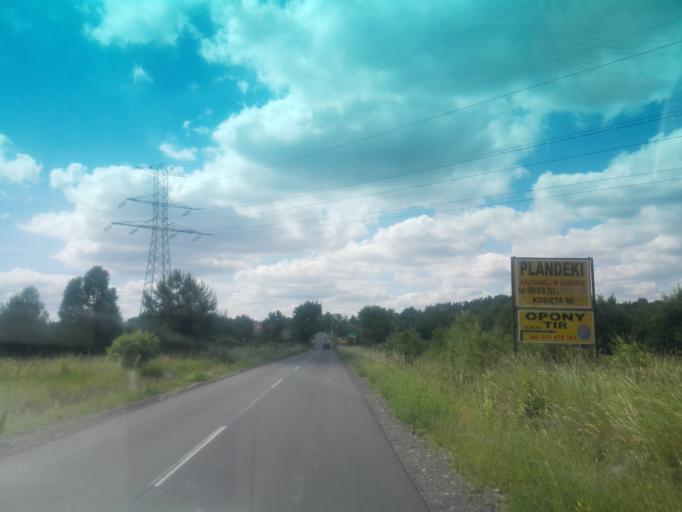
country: PL
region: Silesian Voivodeship
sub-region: Powiat czestochowski
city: Olsztyn
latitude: 50.7804
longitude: 19.2736
